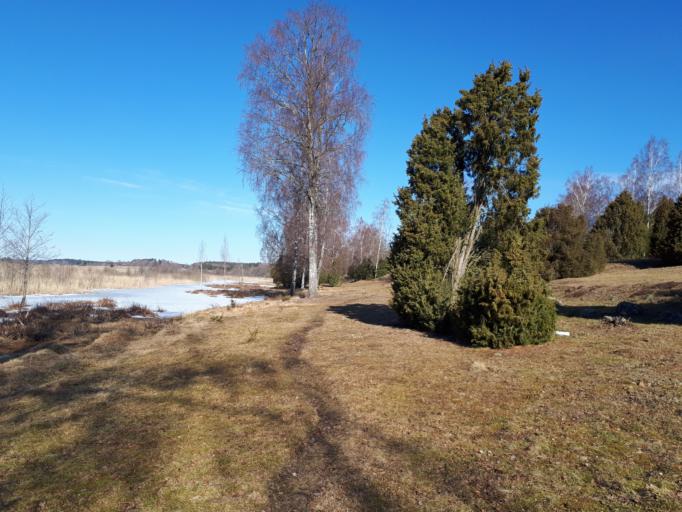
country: SE
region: Soedermanland
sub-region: Flens Kommun
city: Halleforsnas
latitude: 59.0775
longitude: 16.3705
